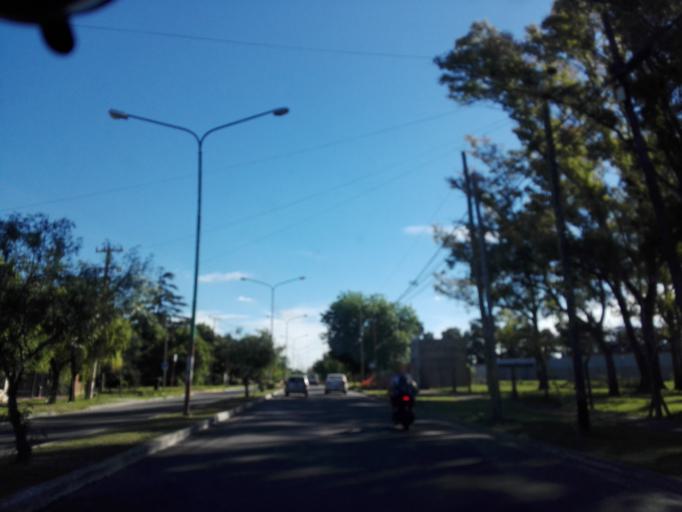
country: AR
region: Buenos Aires
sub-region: Partido de La Plata
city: La Plata
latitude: -34.8874
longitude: -58.0038
